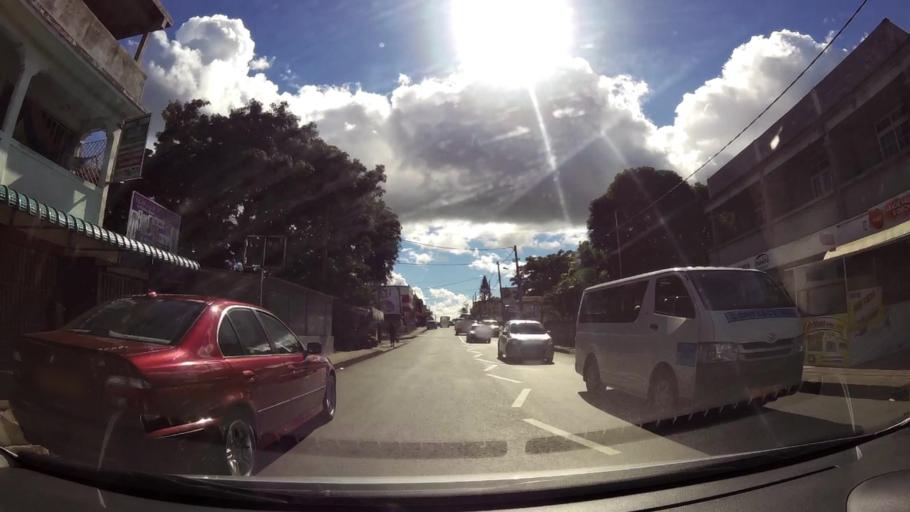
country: MU
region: Pamplemousses
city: Le Hochet
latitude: -20.1337
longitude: 57.5281
